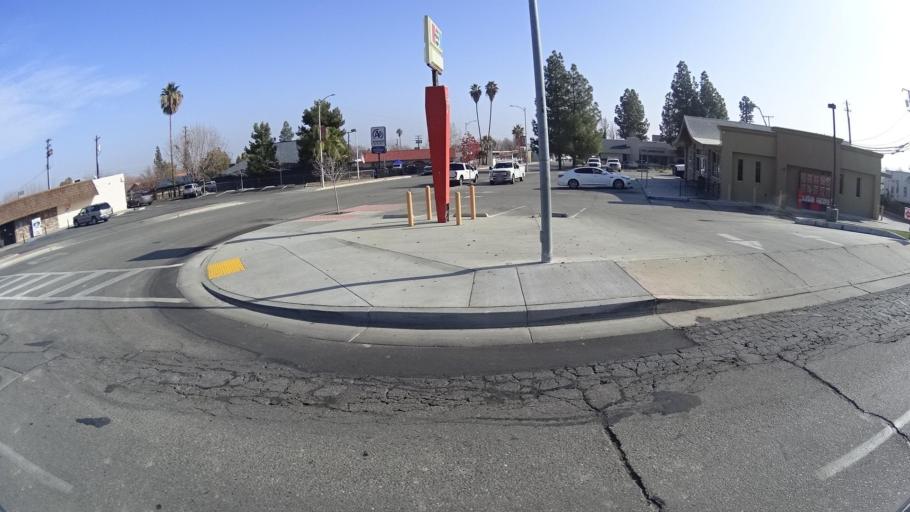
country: US
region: California
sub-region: Kern County
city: Taft
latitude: 35.1426
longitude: -119.4652
